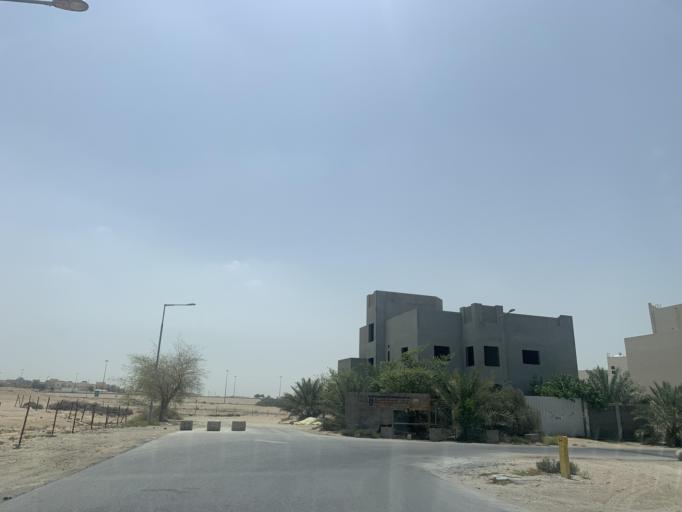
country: BH
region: Central Governorate
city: Madinat Hamad
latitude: 26.1452
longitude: 50.5062
